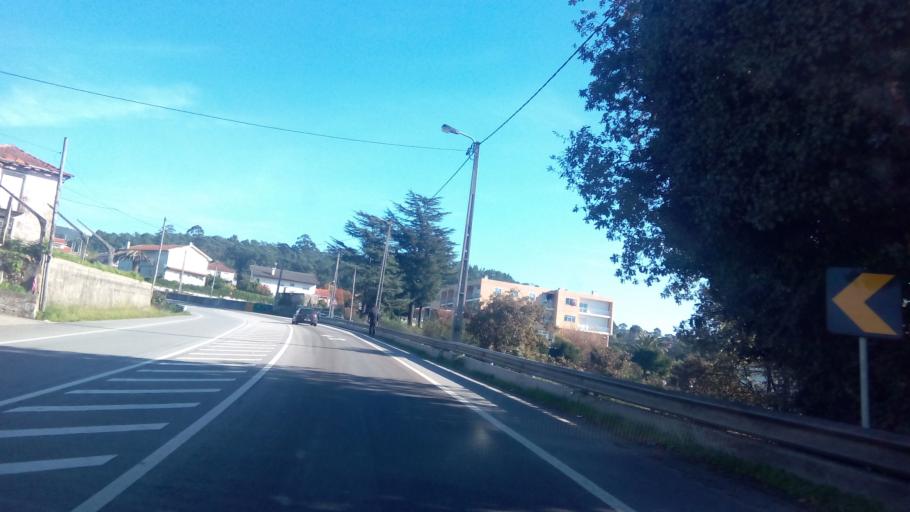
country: PT
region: Porto
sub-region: Paredes
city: Gandra
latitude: 41.1955
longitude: -8.4279
